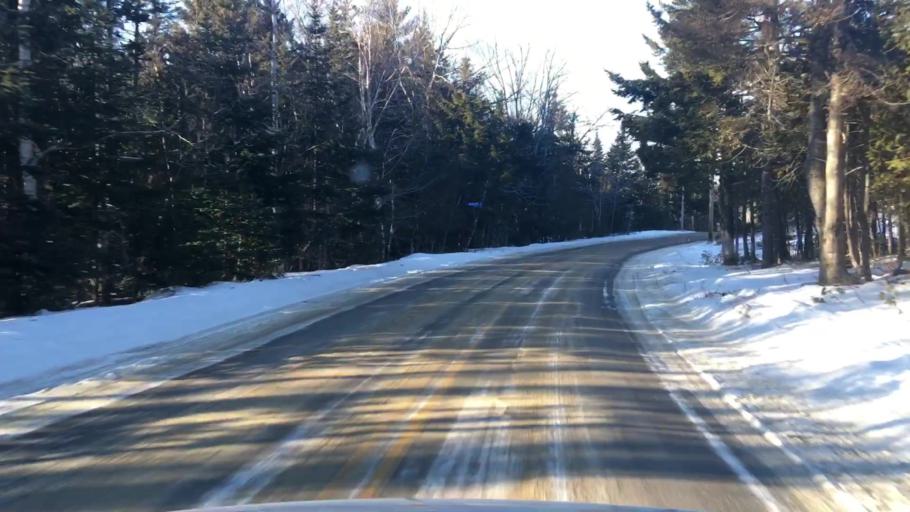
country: US
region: Maine
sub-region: Hancock County
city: Castine
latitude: 44.3669
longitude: -68.7529
